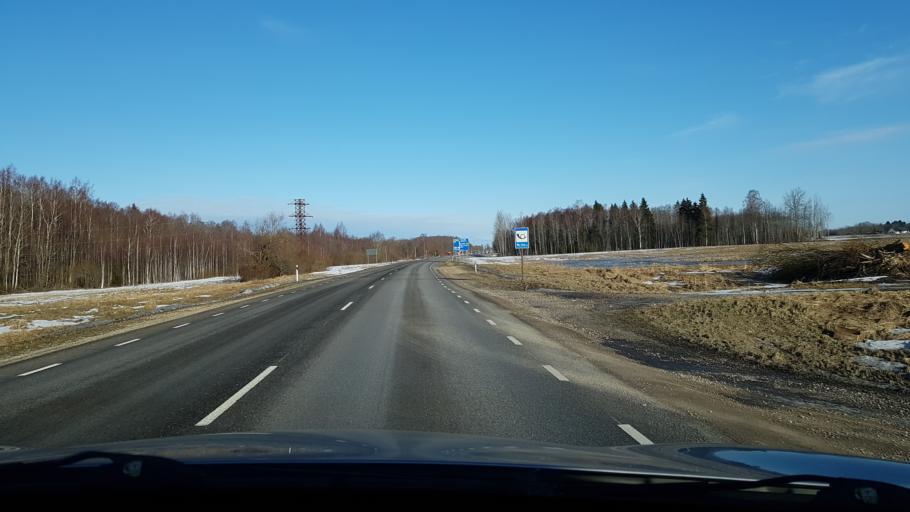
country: EE
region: Viljandimaa
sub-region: Vohma linn
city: Vohma
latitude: 58.6236
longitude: 25.5690
